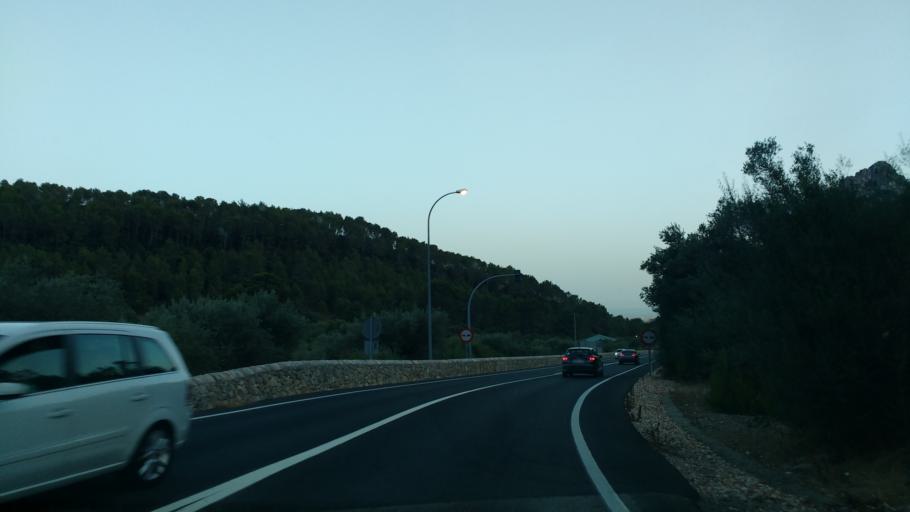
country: ES
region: Balearic Islands
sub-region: Illes Balears
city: Bunyola
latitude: 39.7157
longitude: 2.6904
